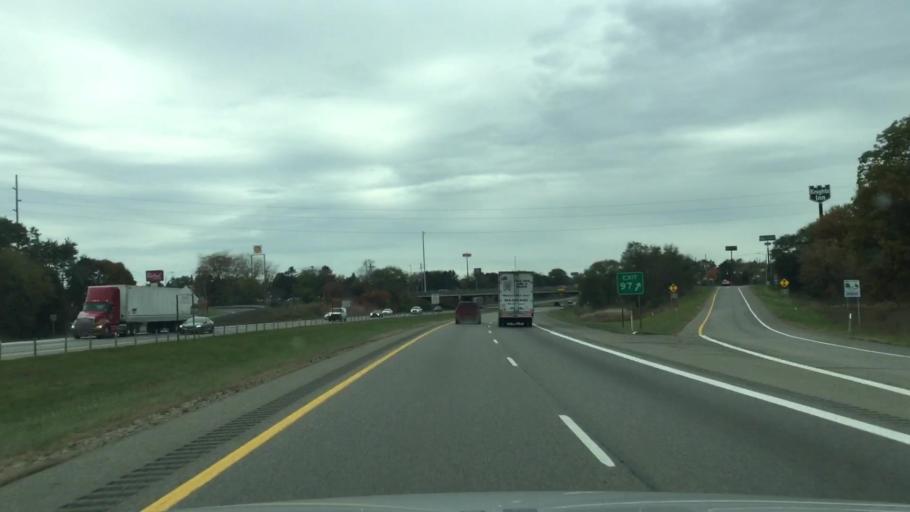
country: US
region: Michigan
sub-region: Calhoun County
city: Lakeview
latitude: 42.2621
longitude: -85.1943
